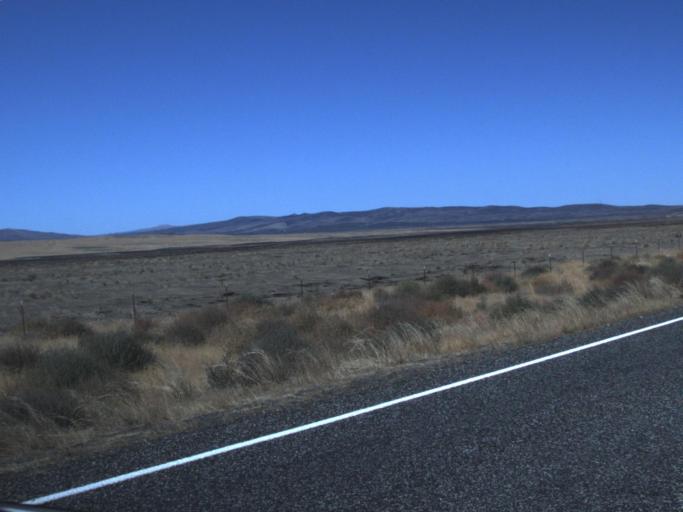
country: US
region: Washington
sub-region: Grant County
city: Desert Aire
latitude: 46.5296
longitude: -119.6811
